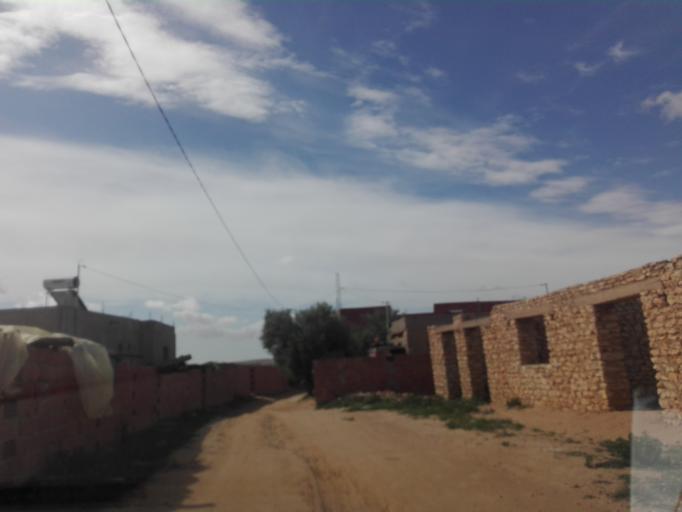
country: TN
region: Safaqis
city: Sfax
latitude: 34.7419
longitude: 10.5087
